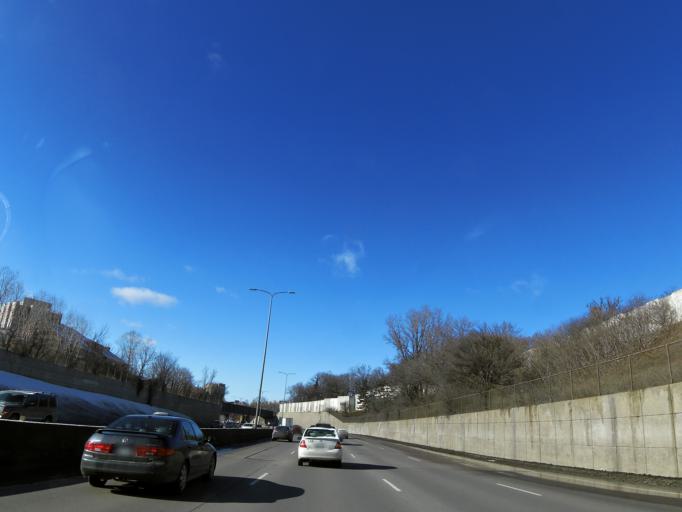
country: US
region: Minnesota
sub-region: Ramsey County
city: Lauderdale
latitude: 44.9650
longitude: -93.2162
